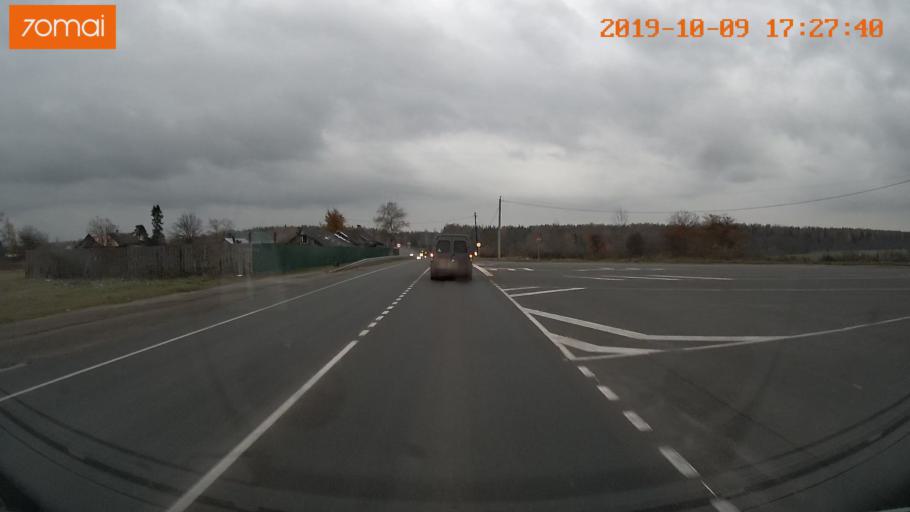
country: RU
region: Ivanovo
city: Furmanov
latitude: 57.1646
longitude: 41.0701
